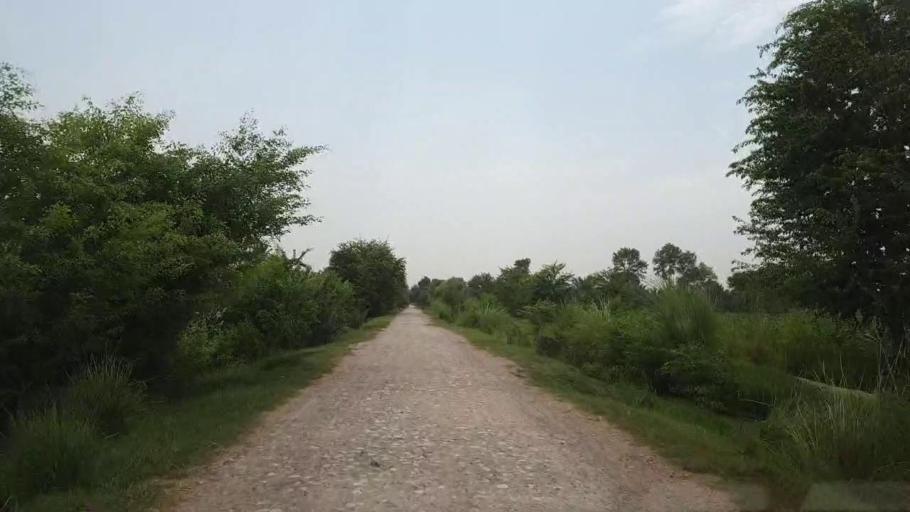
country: PK
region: Sindh
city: Pir jo Goth
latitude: 27.4926
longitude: 68.5976
